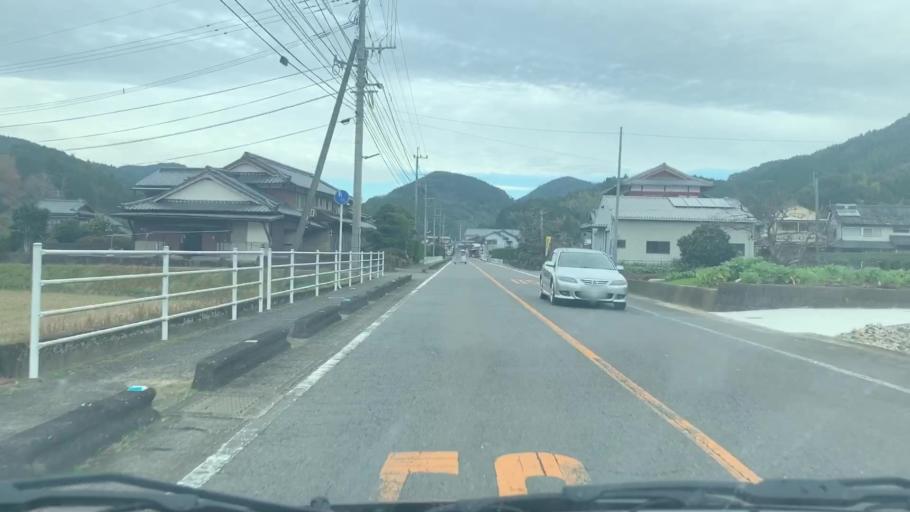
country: JP
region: Saga Prefecture
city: Ureshinomachi-shimojuku
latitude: 33.1447
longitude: 129.9764
